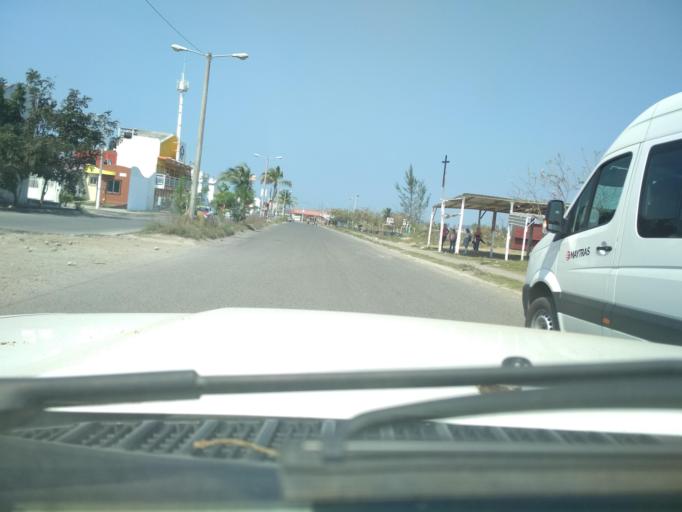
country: MX
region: Veracruz
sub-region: Veracruz
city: Los Torrentes
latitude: 19.1995
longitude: -96.2080
